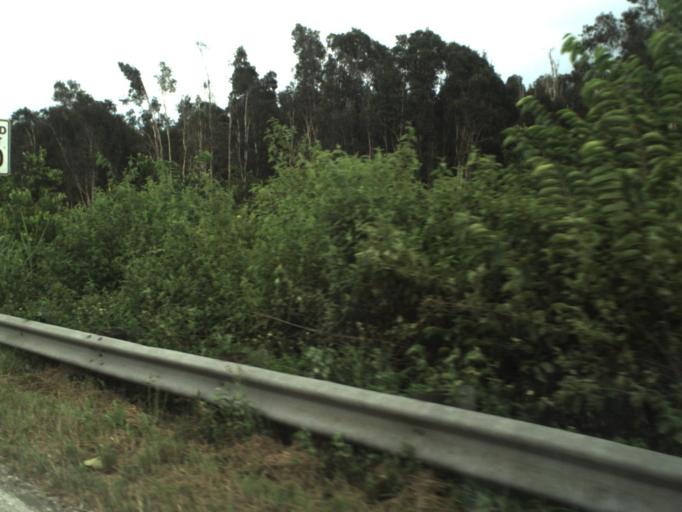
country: US
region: Florida
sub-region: Miami-Dade County
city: Kendall West
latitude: 25.7251
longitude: -80.4800
